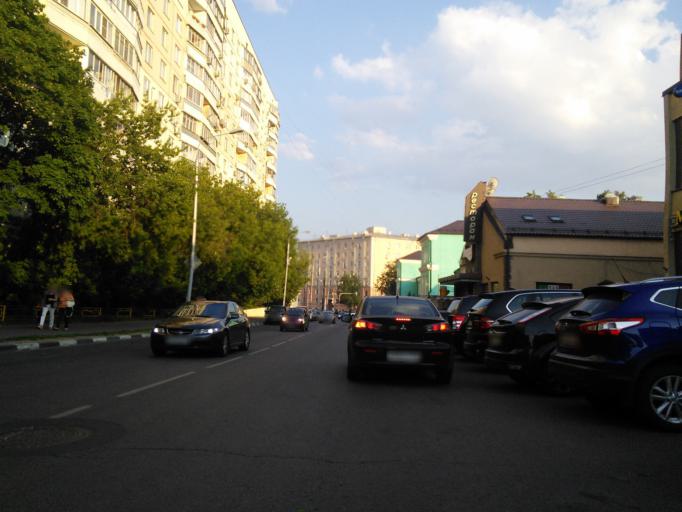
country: RU
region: Moscow
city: Sokol'niki
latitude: 55.7872
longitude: 37.6752
